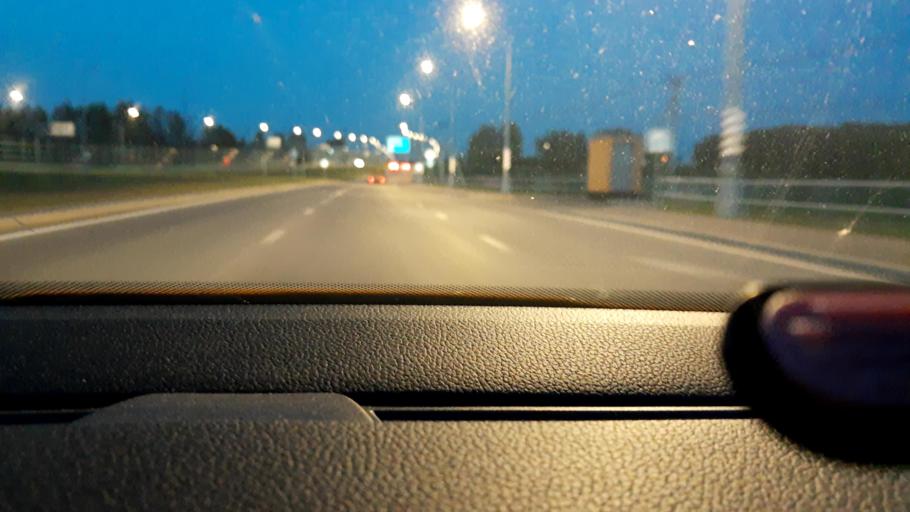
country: RU
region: Moskovskaya
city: Filimonki
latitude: 55.5594
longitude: 37.3355
